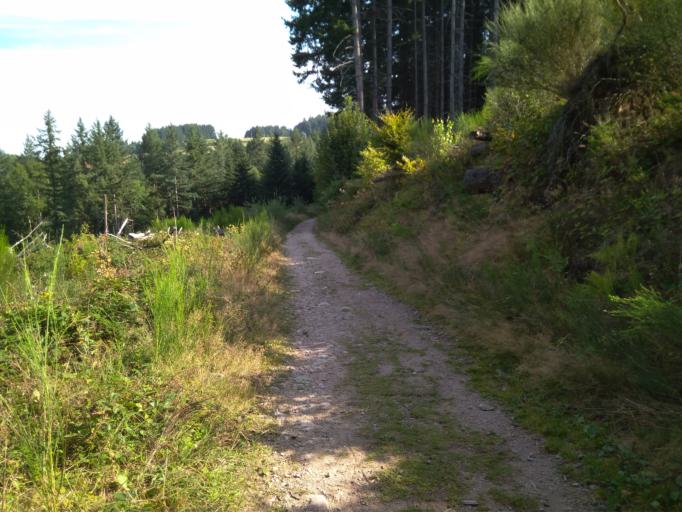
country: FR
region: Auvergne
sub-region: Departement de l'Allier
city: Le Mayet-de-Montagne
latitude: 46.1286
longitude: 3.7627
